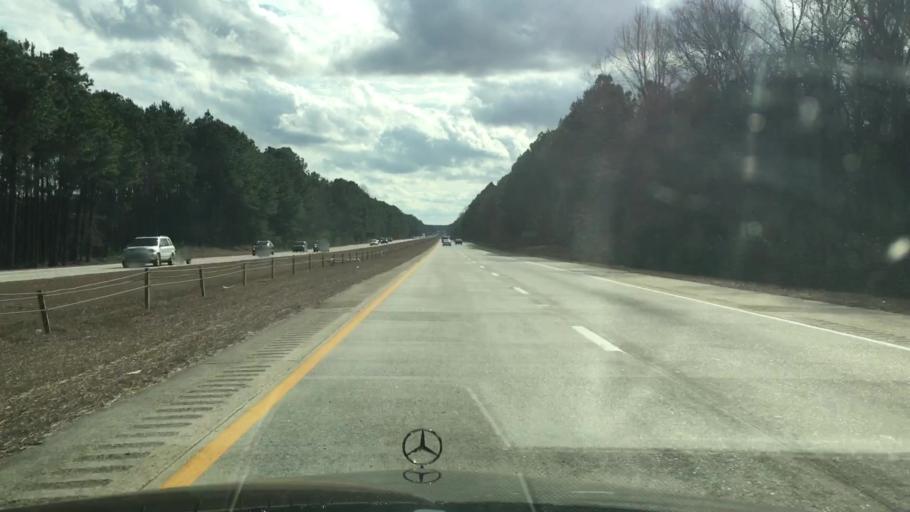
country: US
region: North Carolina
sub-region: Johnston County
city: Benson
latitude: 35.5061
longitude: -78.5552
